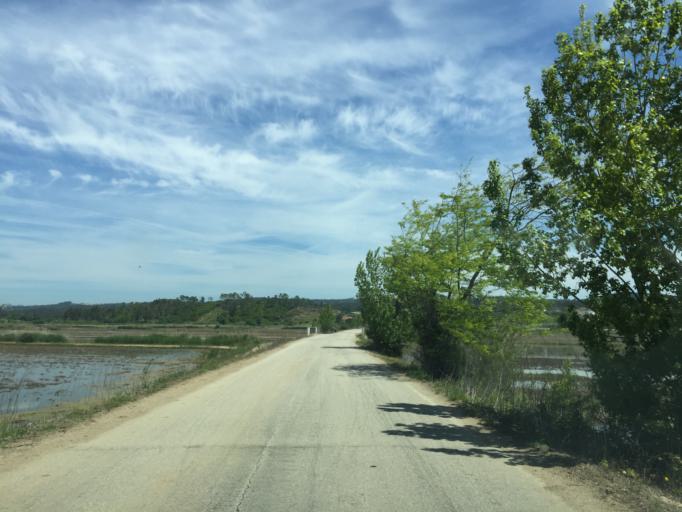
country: PT
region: Leiria
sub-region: Pombal
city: Lourical
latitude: 40.0701
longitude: -8.7421
